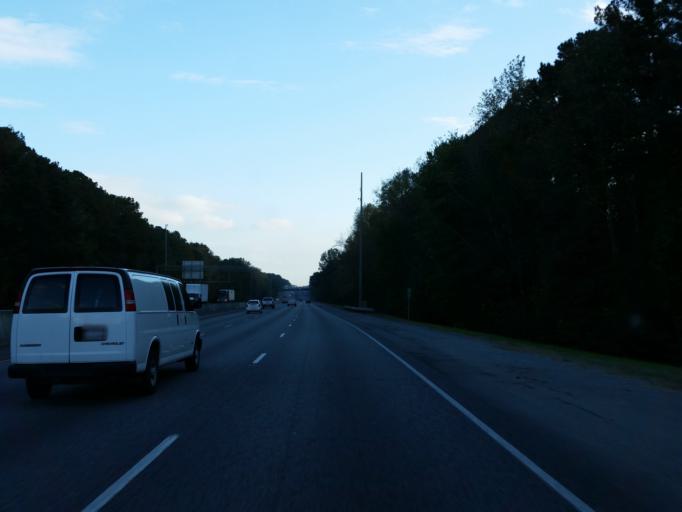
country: US
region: Georgia
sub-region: Bibb County
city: West Point
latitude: 32.9436
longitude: -83.8118
